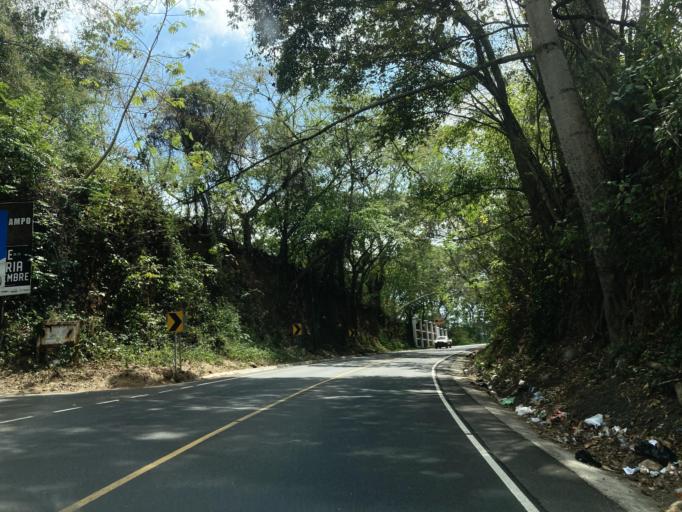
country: GT
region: Santa Rosa
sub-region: Municipio de Taxisco
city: Taxisco
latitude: 14.0751
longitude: -90.4768
